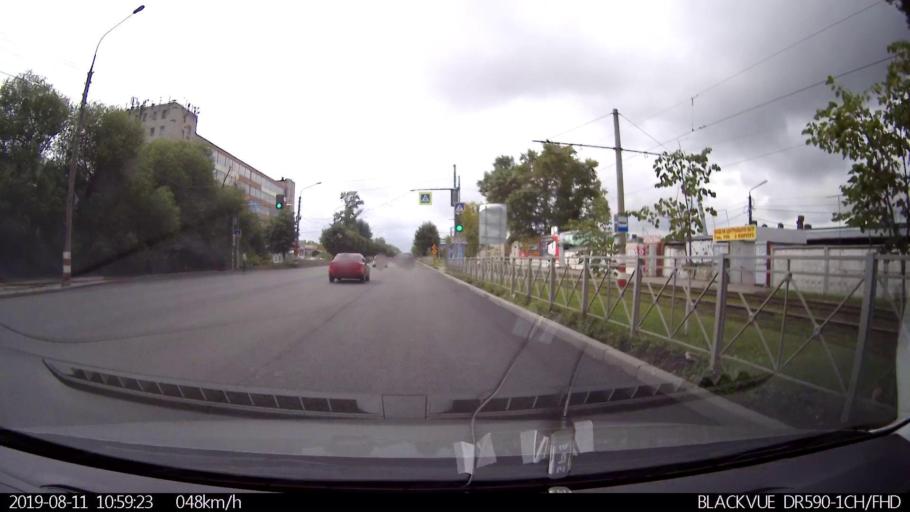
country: RU
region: Ulyanovsk
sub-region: Ulyanovskiy Rayon
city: Ulyanovsk
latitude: 54.2506
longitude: 48.3157
